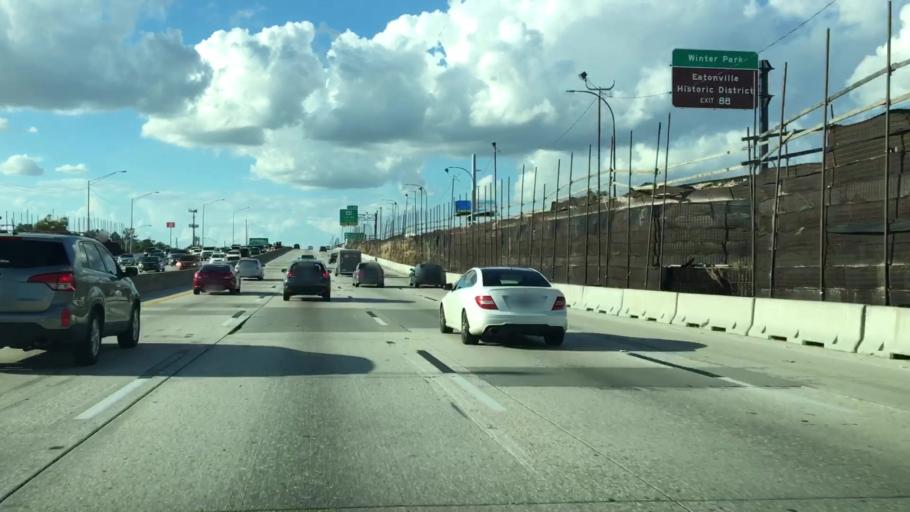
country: US
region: Florida
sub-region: Orange County
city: Fairview Shores
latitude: 28.5911
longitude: -81.3796
